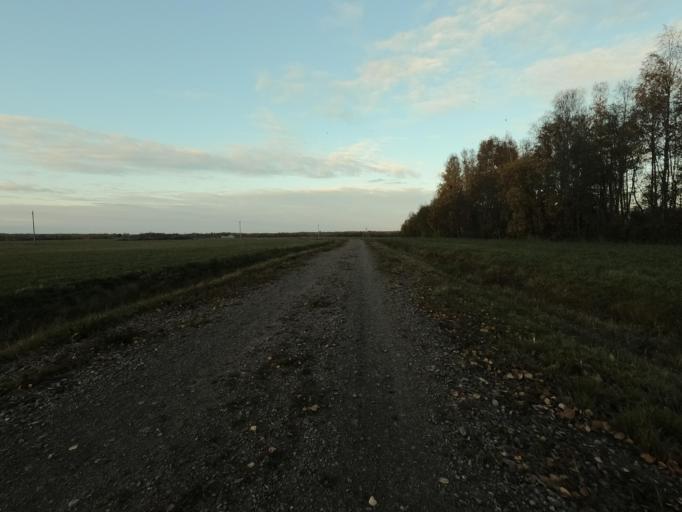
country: RU
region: Leningrad
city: Mga
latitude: 59.7849
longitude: 31.1972
